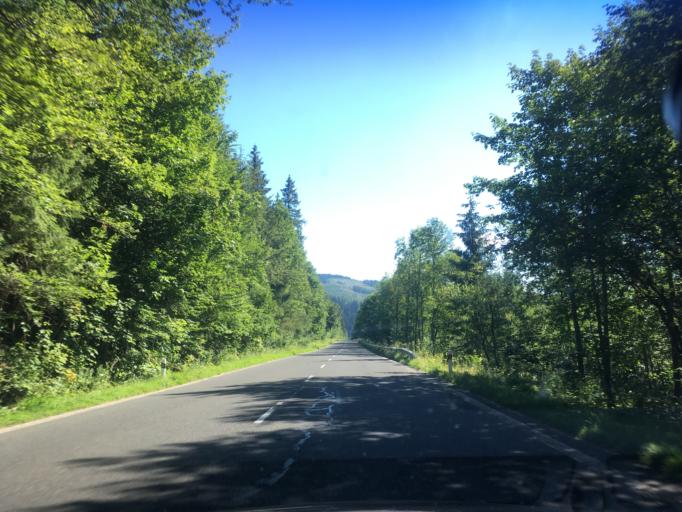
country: PL
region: Lesser Poland Voivodeship
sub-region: Powiat tatrzanski
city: Bukowina Tatrzanska
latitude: 49.2741
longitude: 20.1590
